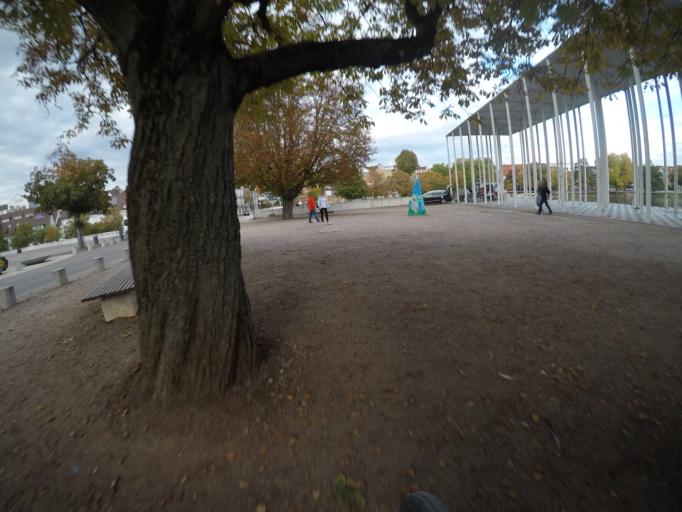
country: DE
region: Baden-Wuerttemberg
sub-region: Regierungsbezirk Stuttgart
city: Boeblingen
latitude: 48.6829
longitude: 9.0119
